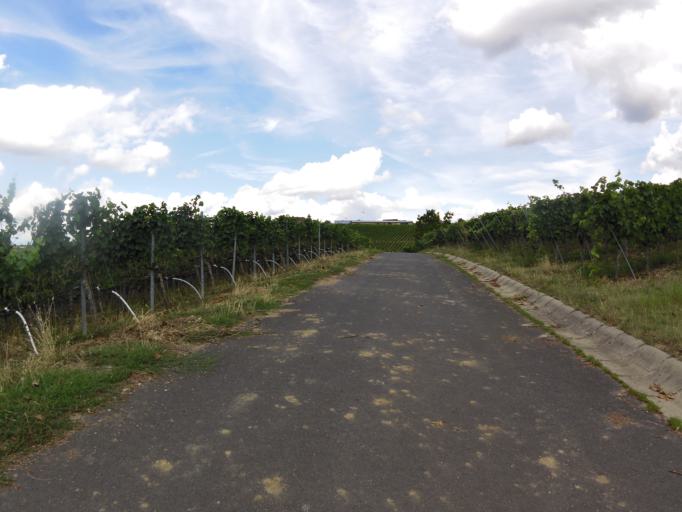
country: DE
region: Bavaria
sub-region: Regierungsbezirk Unterfranken
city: Sommerhausen
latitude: 49.6955
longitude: 10.0325
